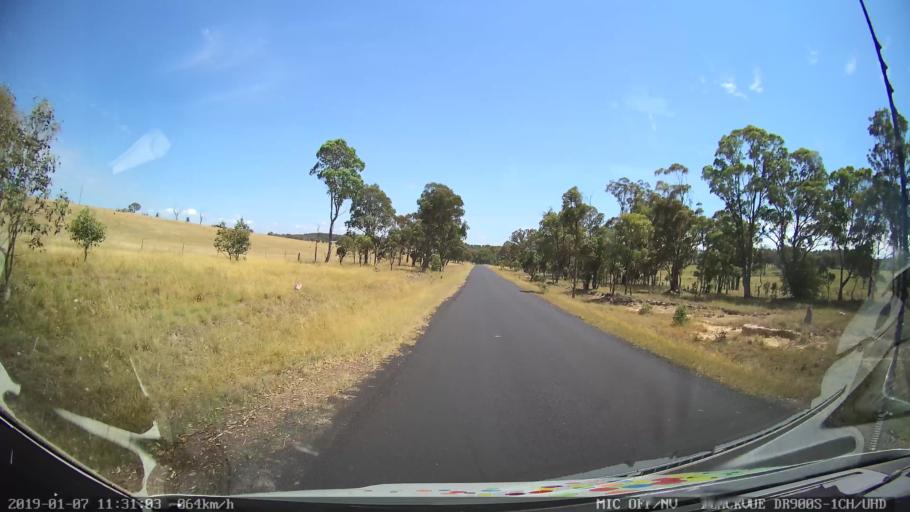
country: AU
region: New South Wales
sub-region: Armidale Dumaresq
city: Armidale
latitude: -30.4236
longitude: 151.5637
